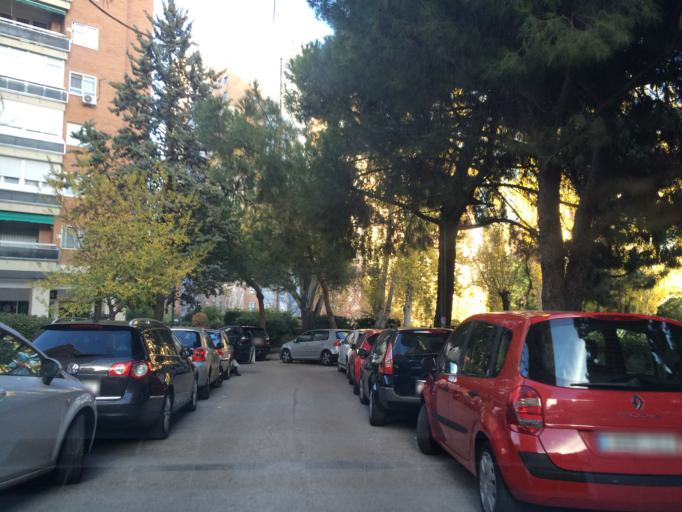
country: ES
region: Madrid
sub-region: Provincia de Madrid
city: Pinar de Chamartin
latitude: 40.4803
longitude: -3.6690
